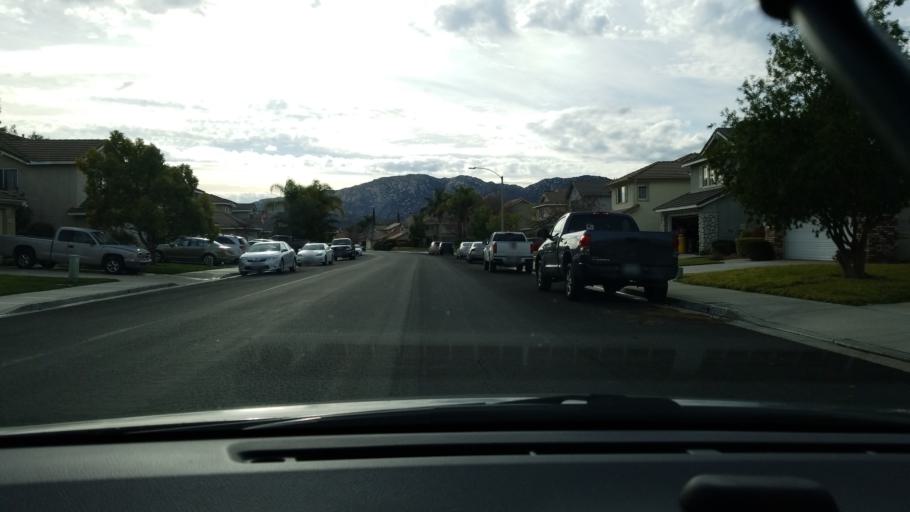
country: US
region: California
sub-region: Riverside County
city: Temecula
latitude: 33.4738
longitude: -117.1073
